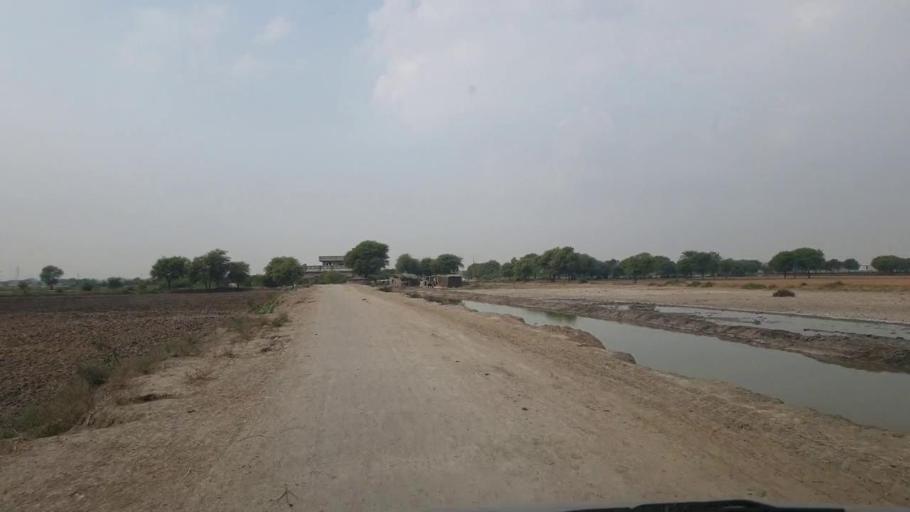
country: PK
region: Sindh
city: Talhar
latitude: 24.8634
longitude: 68.8222
